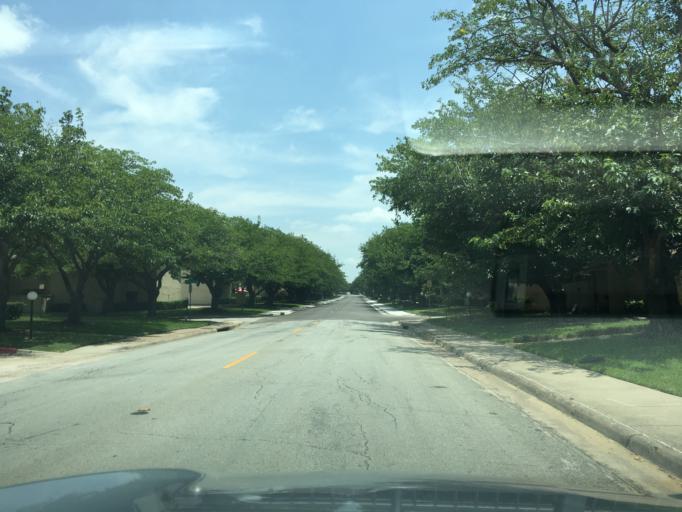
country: US
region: Texas
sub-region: Dallas County
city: Addison
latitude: 32.9224
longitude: -96.8083
